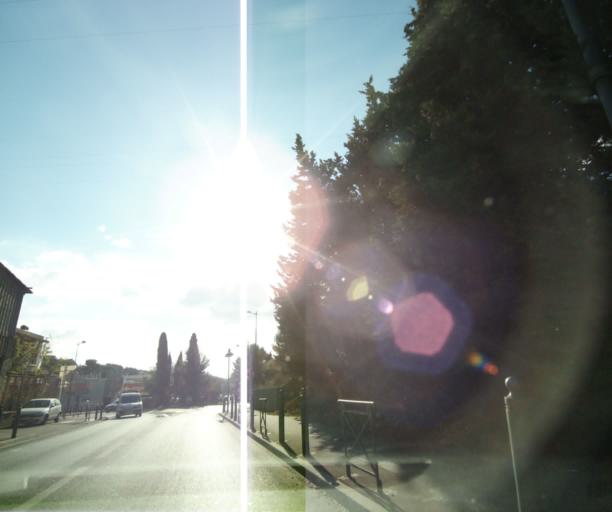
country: FR
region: Provence-Alpes-Cote d'Azur
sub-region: Departement des Bouches-du-Rhone
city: Septemes-les-Vallons
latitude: 43.3925
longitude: 5.3641
